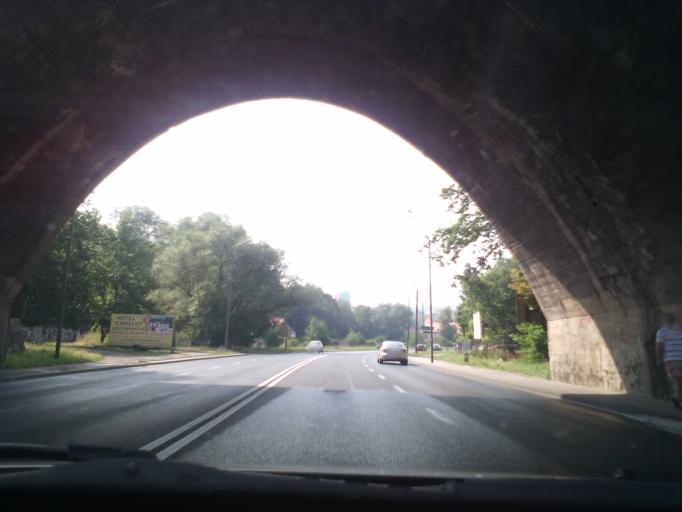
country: PL
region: Lower Silesian Voivodeship
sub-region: Powiat walbrzyski
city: Szczawno-Zdroj
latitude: 50.8167
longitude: 16.2770
